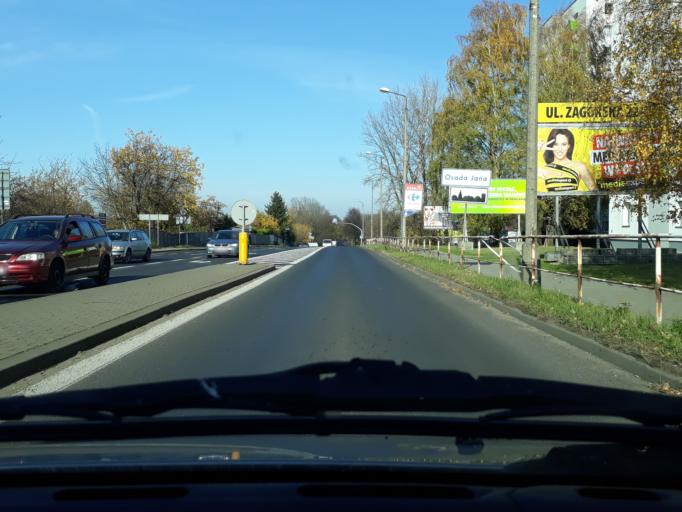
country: PL
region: Silesian Voivodeship
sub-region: Powiat tarnogorski
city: Tarnowskie Gory
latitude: 50.4317
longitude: 18.8660
